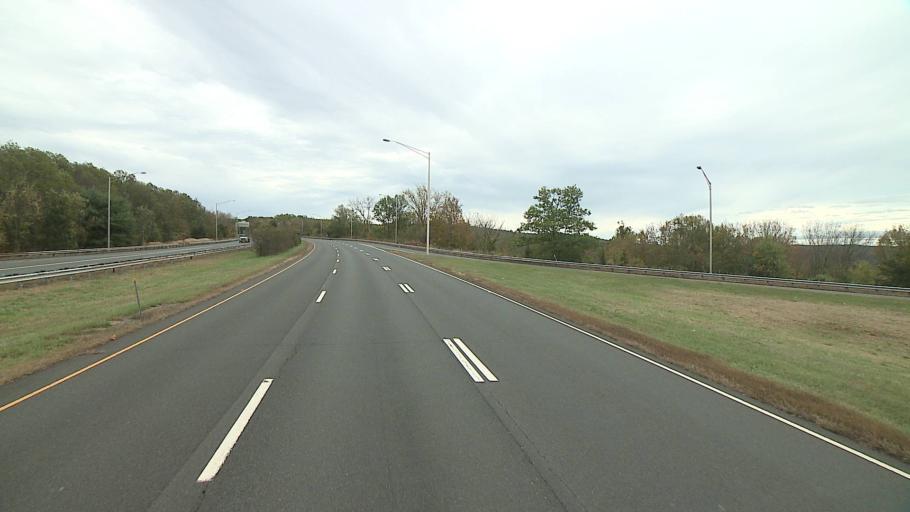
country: US
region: Connecticut
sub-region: Middlesex County
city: Middletown
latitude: 41.5317
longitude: -72.6175
